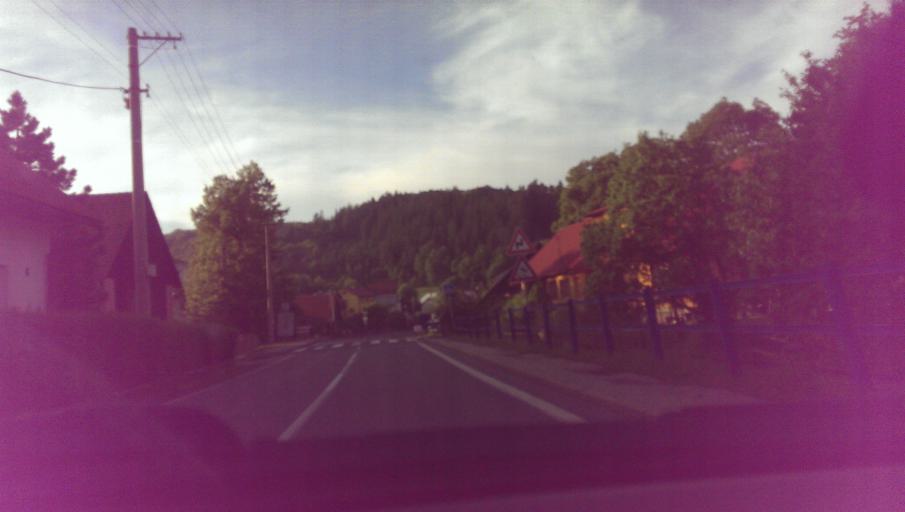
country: CZ
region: Zlin
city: Valasska Polanka
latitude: 49.2359
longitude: 17.9543
